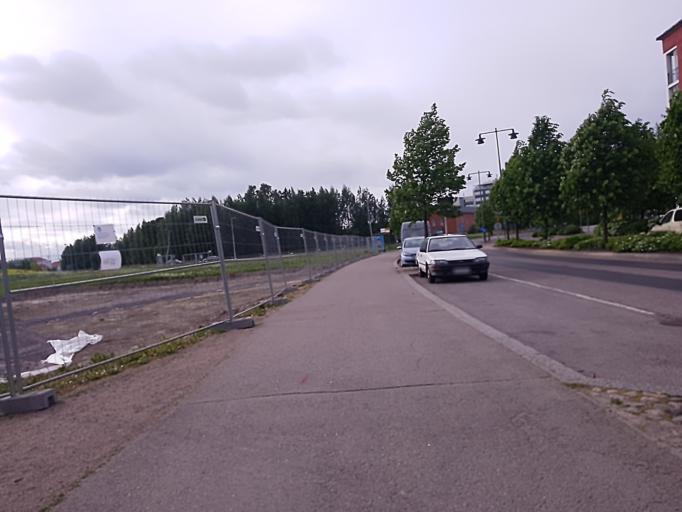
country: FI
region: Uusimaa
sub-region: Helsinki
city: Vantaa
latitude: 60.2855
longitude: 24.9582
